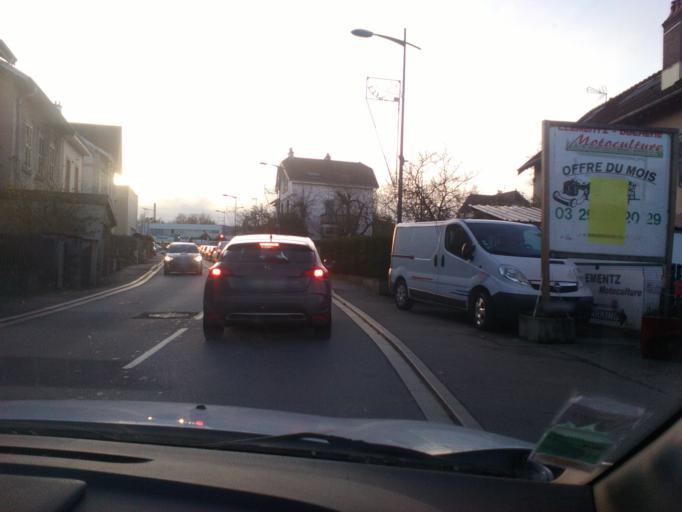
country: FR
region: Lorraine
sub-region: Departement des Vosges
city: Golbey
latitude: 48.1930
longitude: 6.4402
